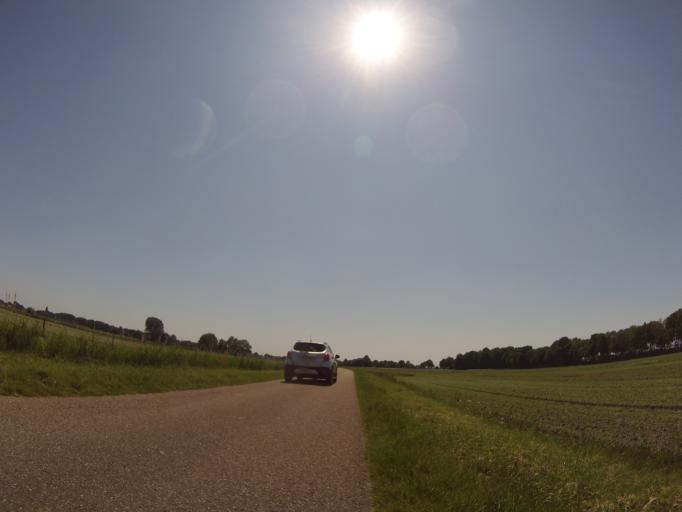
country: NL
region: Drenthe
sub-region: Gemeente Emmen
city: Schoonebeek
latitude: 52.6555
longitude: 6.8775
